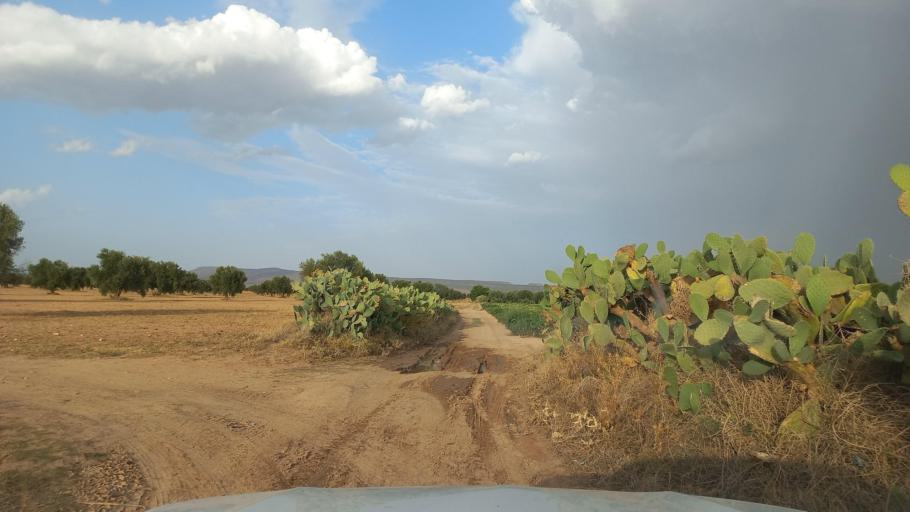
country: TN
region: Al Qasrayn
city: Kasserine
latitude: 35.2829
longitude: 9.0625
